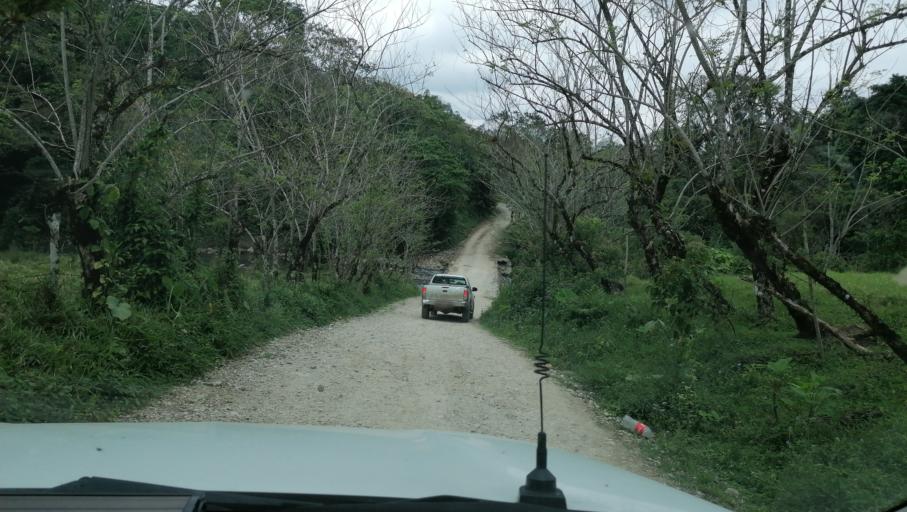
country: MX
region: Chiapas
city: Ocotepec
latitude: 17.2739
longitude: -93.2228
